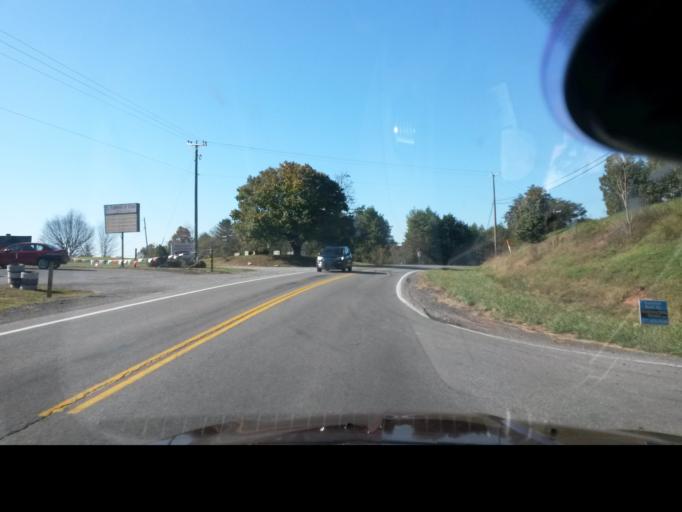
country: US
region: Virginia
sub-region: Franklin County
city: North Shore
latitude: 37.1274
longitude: -79.7636
